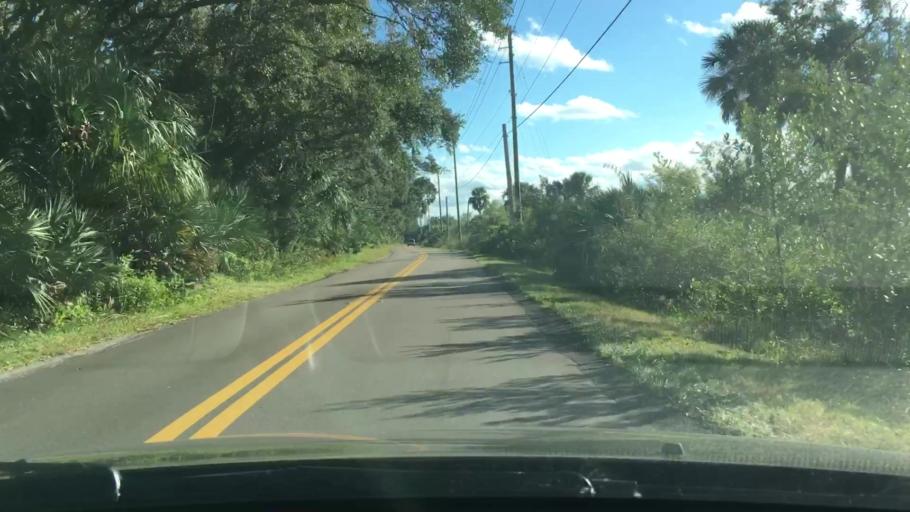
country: US
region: Florida
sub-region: Volusia County
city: Ormond-by-the-Sea
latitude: 29.4034
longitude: -81.0955
